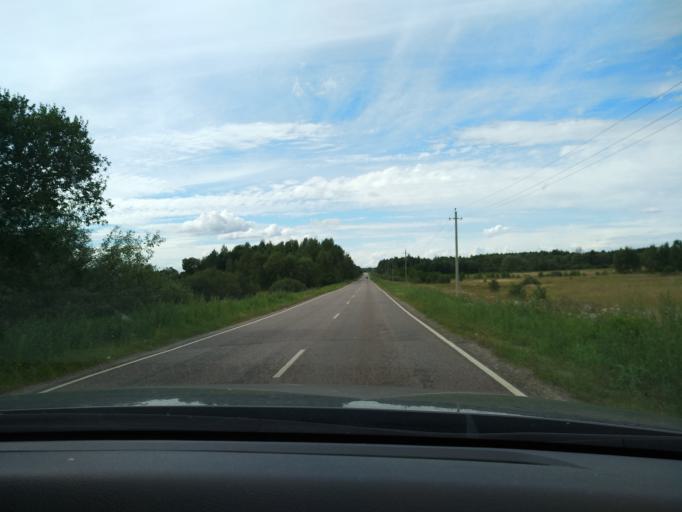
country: RU
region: Moskovskaya
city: Krasnyy Tkach
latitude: 55.3858
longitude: 39.1799
